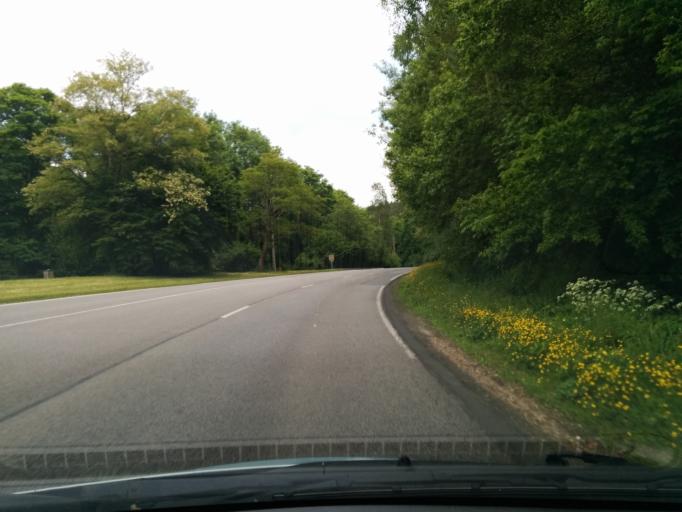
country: FR
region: Haute-Normandie
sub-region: Departement de l'Eure
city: Vernon
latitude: 49.1248
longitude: 1.5003
